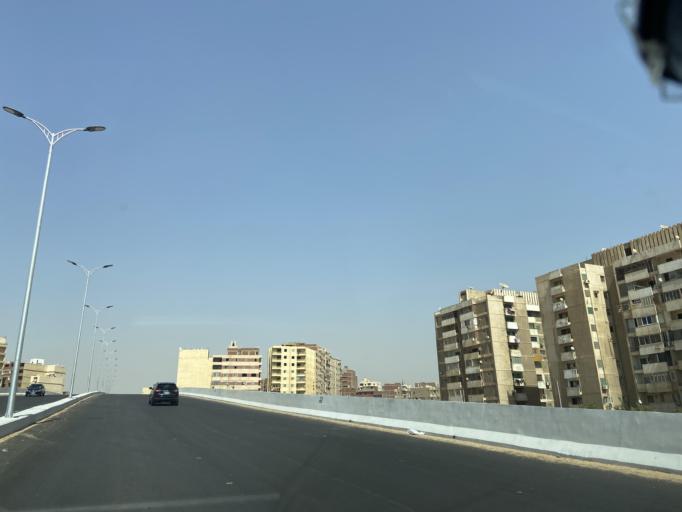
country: EG
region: Muhafazat al Qahirah
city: Cairo
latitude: 30.0611
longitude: 31.3785
